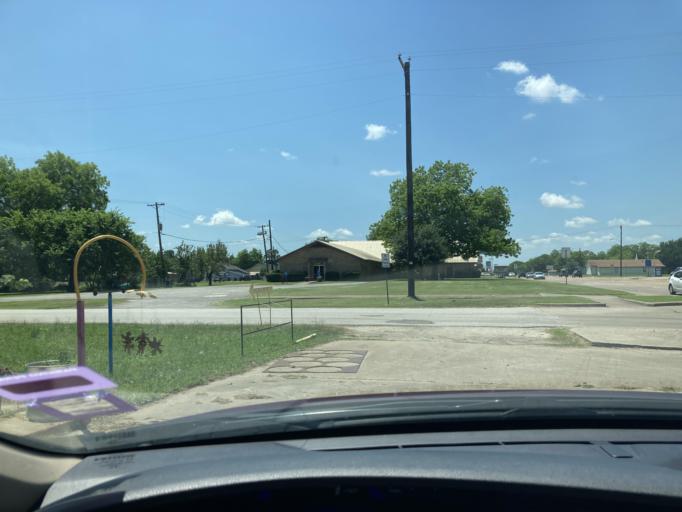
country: US
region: Texas
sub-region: Navarro County
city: Kerens
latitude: 32.1330
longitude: -96.2290
